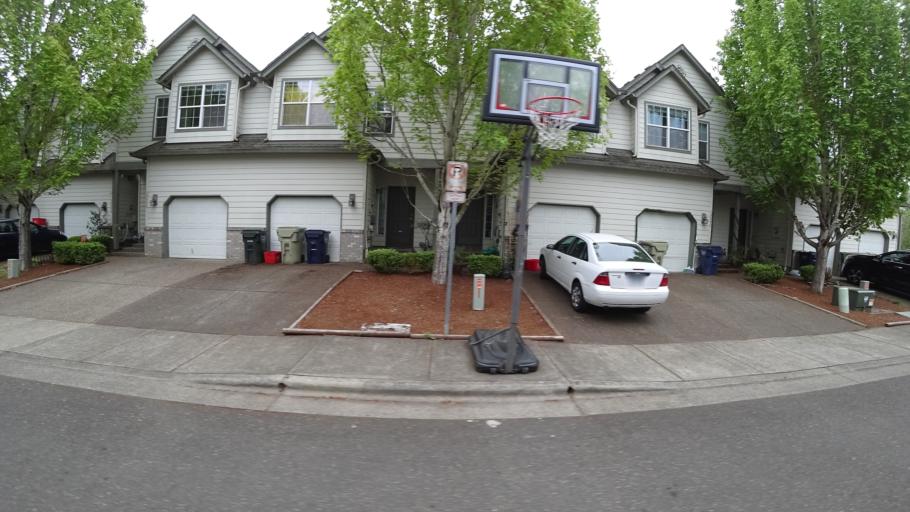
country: US
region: Oregon
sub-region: Washington County
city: Aloha
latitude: 45.5028
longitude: -122.8686
